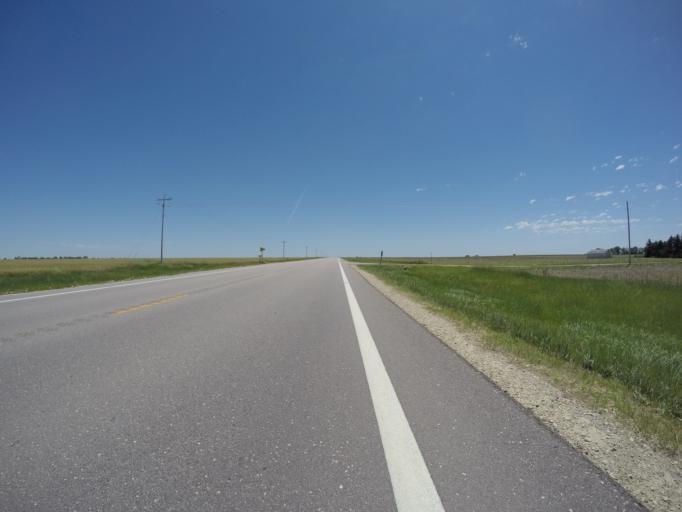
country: US
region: Kansas
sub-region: Republic County
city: Belleville
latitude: 39.8127
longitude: -97.6846
